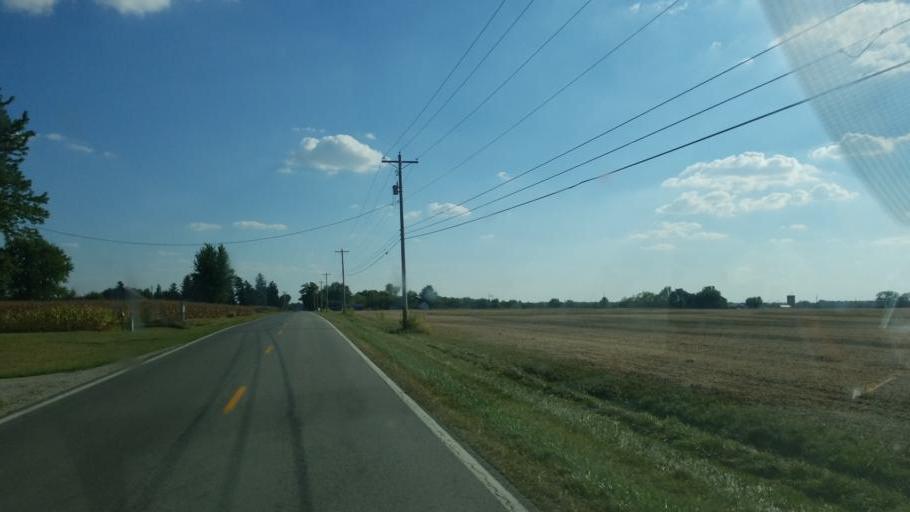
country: US
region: Ohio
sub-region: Union County
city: Richwood
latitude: 40.6042
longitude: -83.3805
